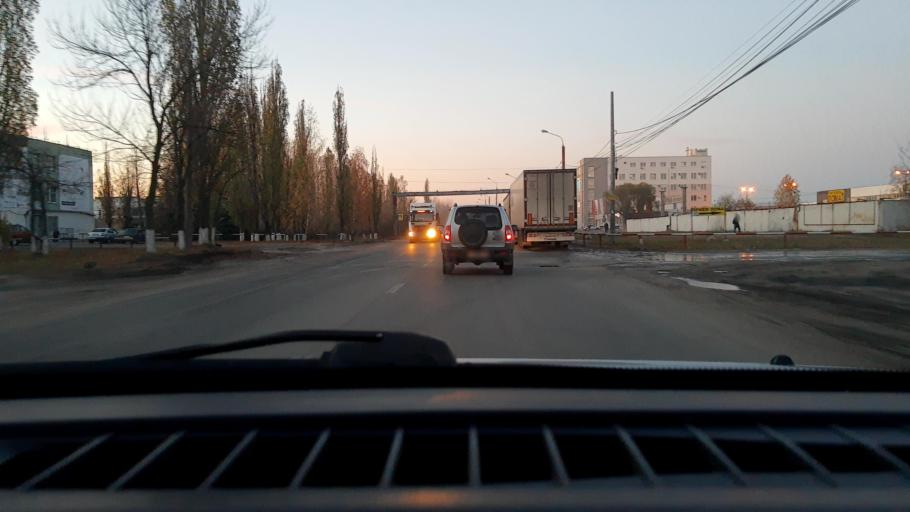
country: RU
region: Nizjnij Novgorod
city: Gorbatovka
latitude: 56.3553
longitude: 43.8046
